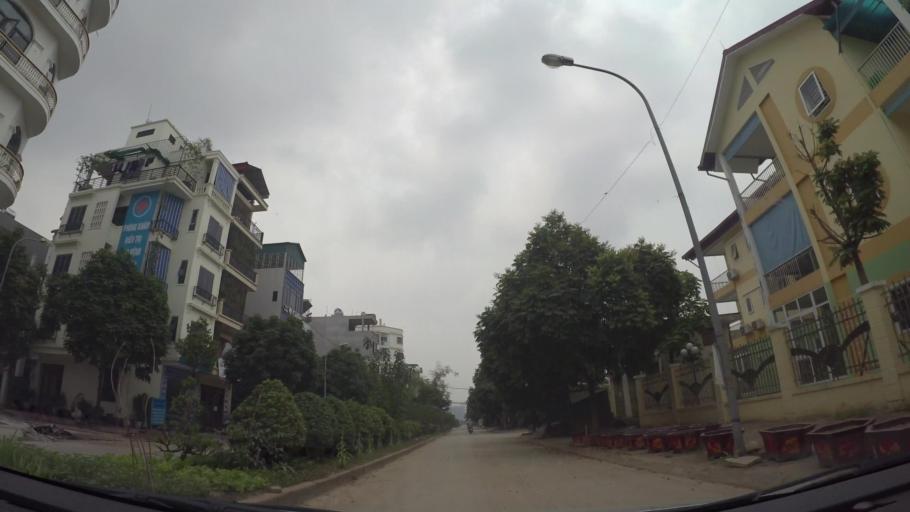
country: VN
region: Ha Noi
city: Ha Dong
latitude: 20.9870
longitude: 105.7507
